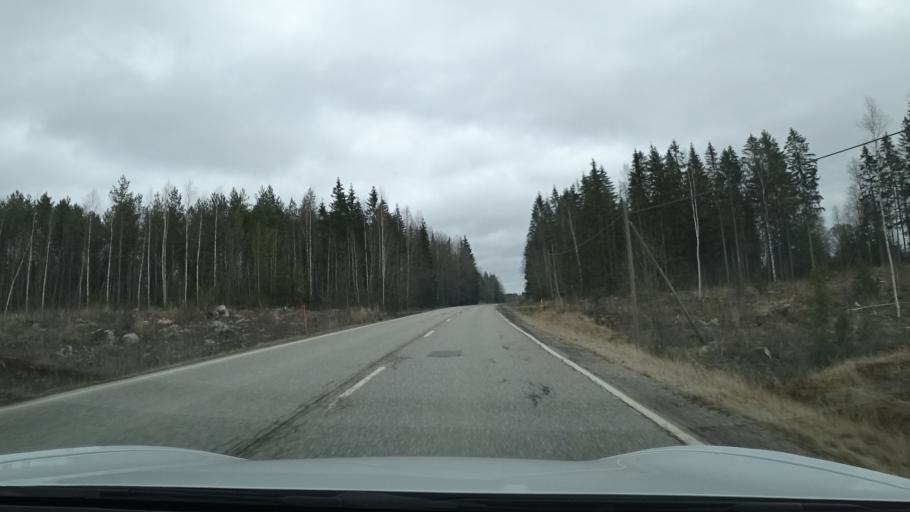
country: FI
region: Uusimaa
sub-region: Porvoo
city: Pukkila
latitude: 60.6595
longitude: 25.6942
